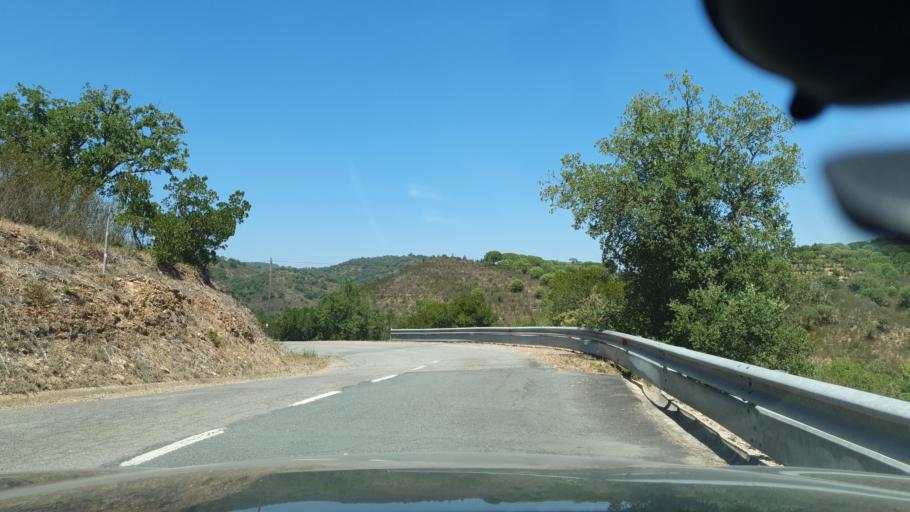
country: PT
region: Beja
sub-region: Odemira
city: Odemira
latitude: 37.6012
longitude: -8.5707
